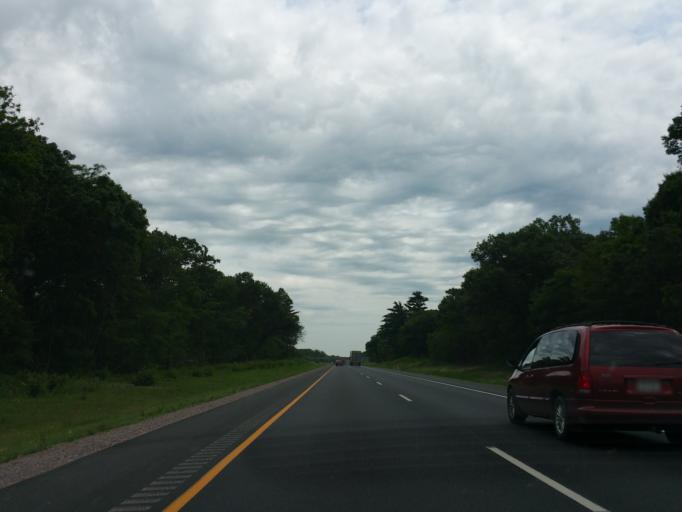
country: US
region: Wisconsin
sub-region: Juneau County
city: Mauston
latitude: 43.7693
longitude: -89.9981
